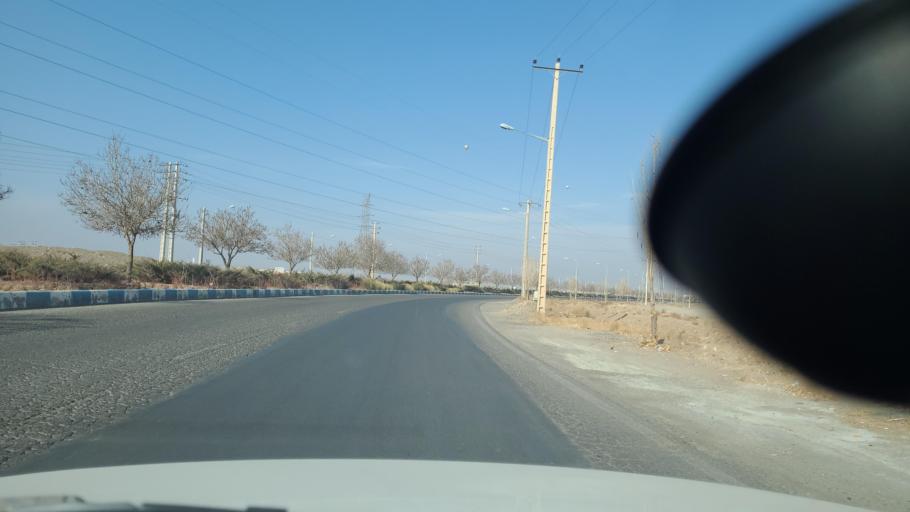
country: IR
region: Razavi Khorasan
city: Fariman
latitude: 35.6999
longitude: 59.8361
